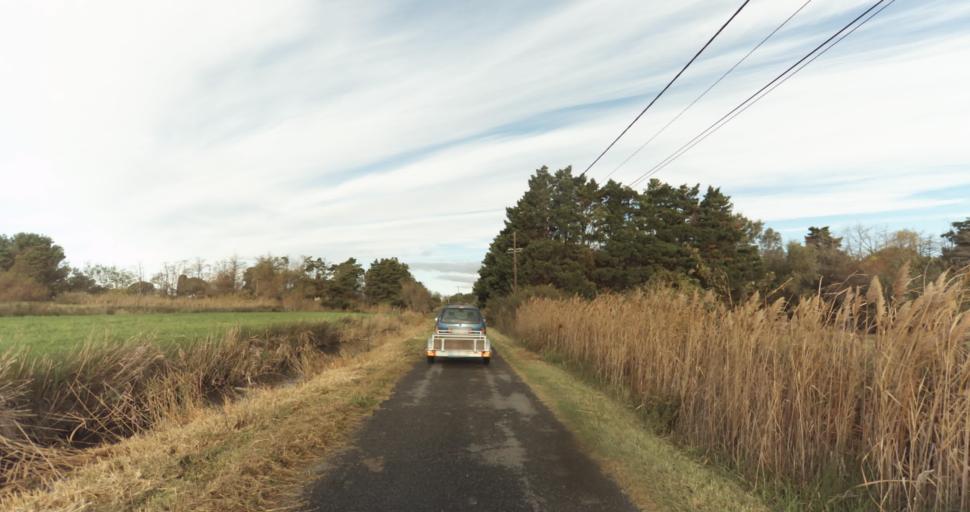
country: FR
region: Languedoc-Roussillon
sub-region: Departement du Gard
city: Aigues-Mortes
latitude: 43.5592
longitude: 4.2022
